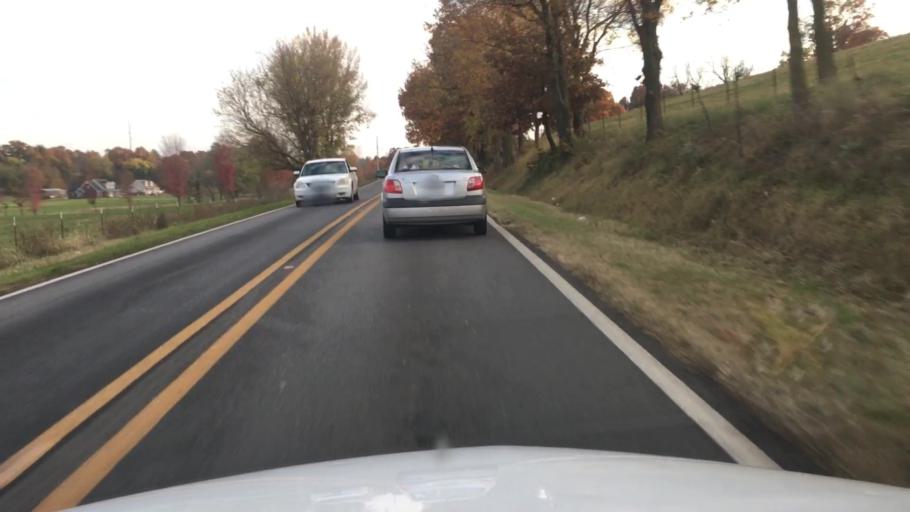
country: US
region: Arkansas
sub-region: Washington County
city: Elm Springs
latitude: 36.1989
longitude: -94.2310
